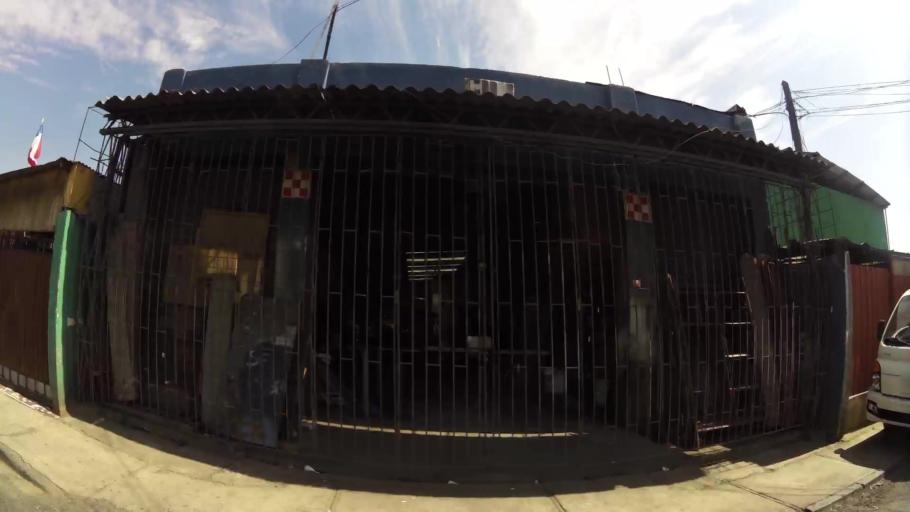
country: CL
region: Santiago Metropolitan
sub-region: Provincia de Santiago
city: La Pintana
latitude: -33.5505
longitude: -70.6534
